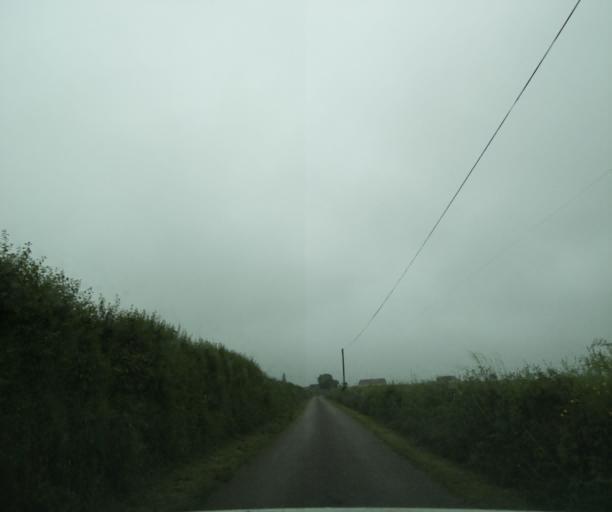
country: FR
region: Bourgogne
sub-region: Departement de Saone-et-Loire
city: Charolles
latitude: 46.4169
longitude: 4.3803
